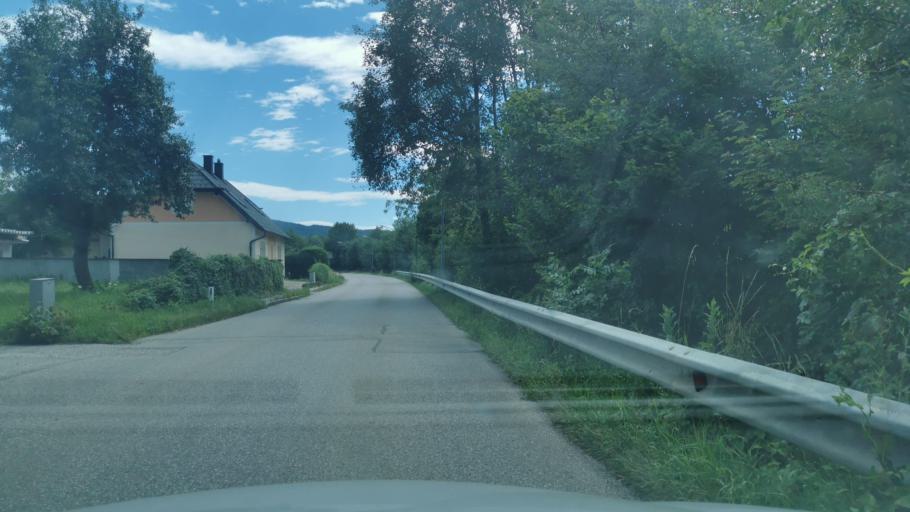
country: AT
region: Lower Austria
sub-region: Politischer Bezirk Sankt Polten
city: Pyhra
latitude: 48.1423
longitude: 15.6402
